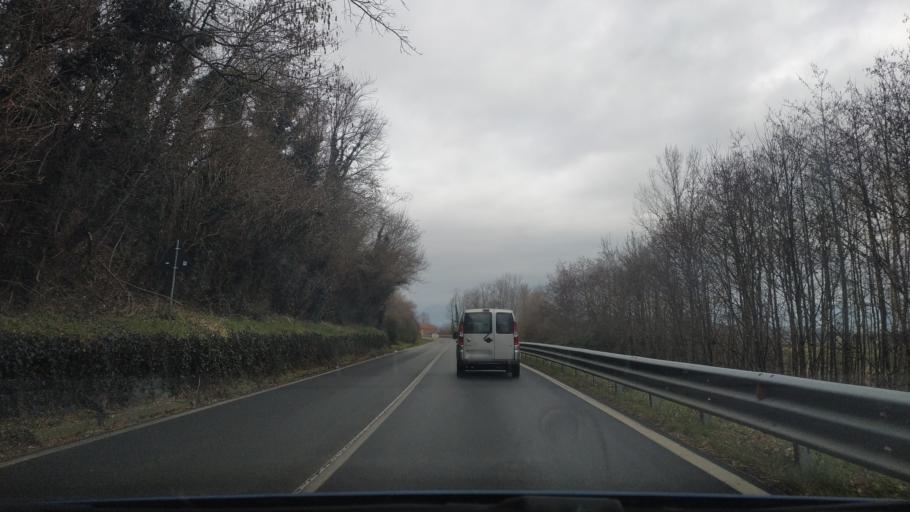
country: IT
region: Piedmont
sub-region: Provincia di Torino
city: Mercenasco
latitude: 45.3564
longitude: 7.8844
